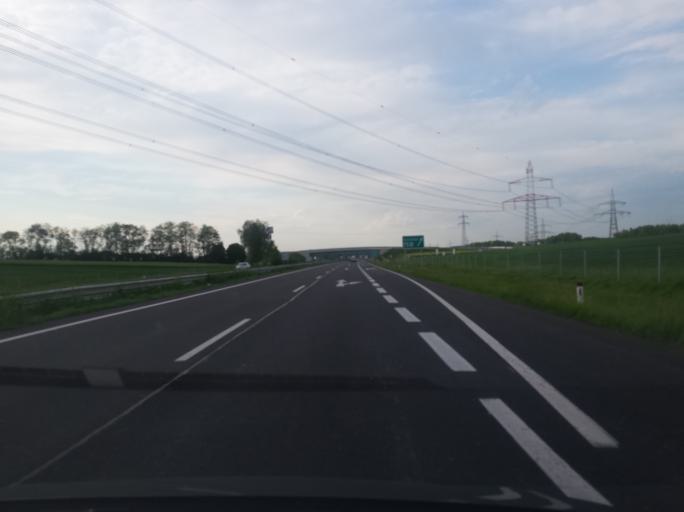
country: AT
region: Burgenland
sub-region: Eisenstadt-Umgebung
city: Hornstein
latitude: 47.8741
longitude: 16.4168
